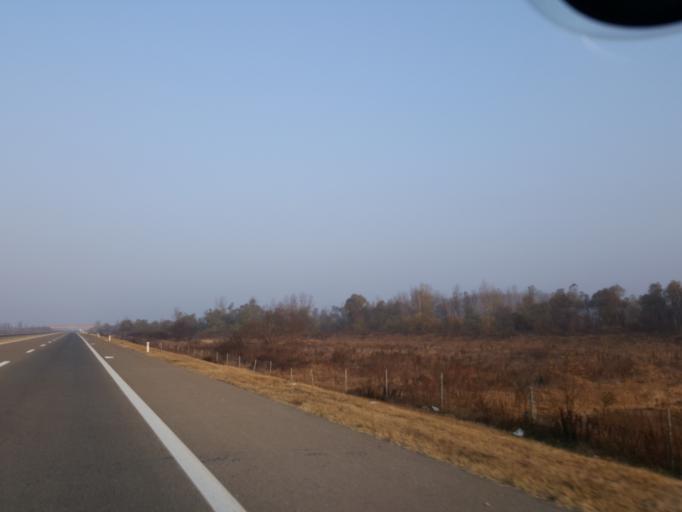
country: RS
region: Central Serbia
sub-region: Jablanicki Okrug
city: Leskovac
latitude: 43.0510
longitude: 21.9819
